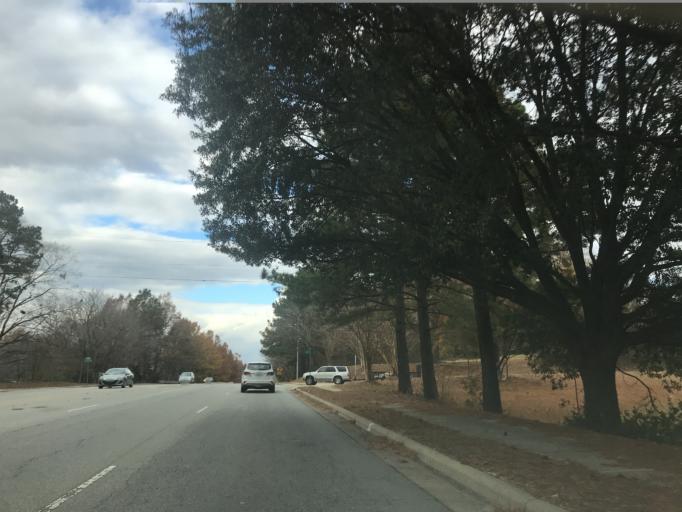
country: US
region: North Carolina
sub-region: Wake County
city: Raleigh
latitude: 35.8380
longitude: -78.5708
